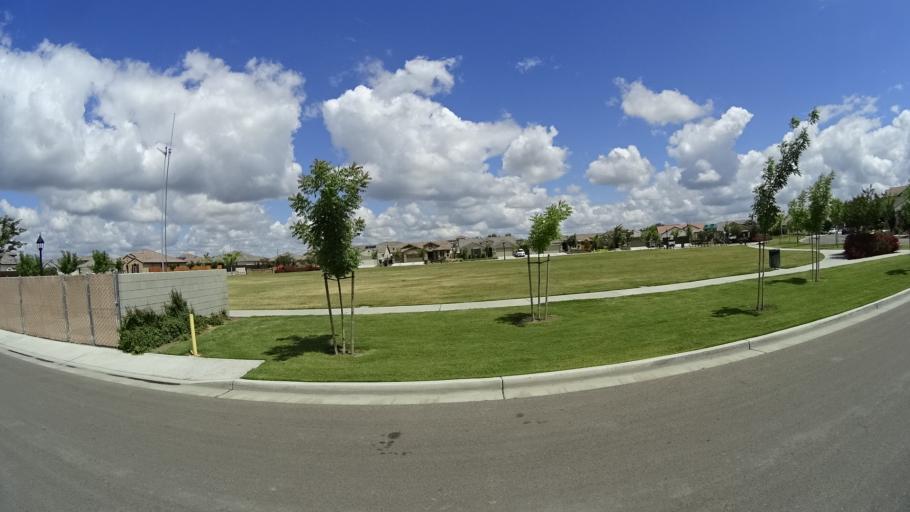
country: US
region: California
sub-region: Kings County
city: Lucerne
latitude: 36.3685
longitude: -119.6614
